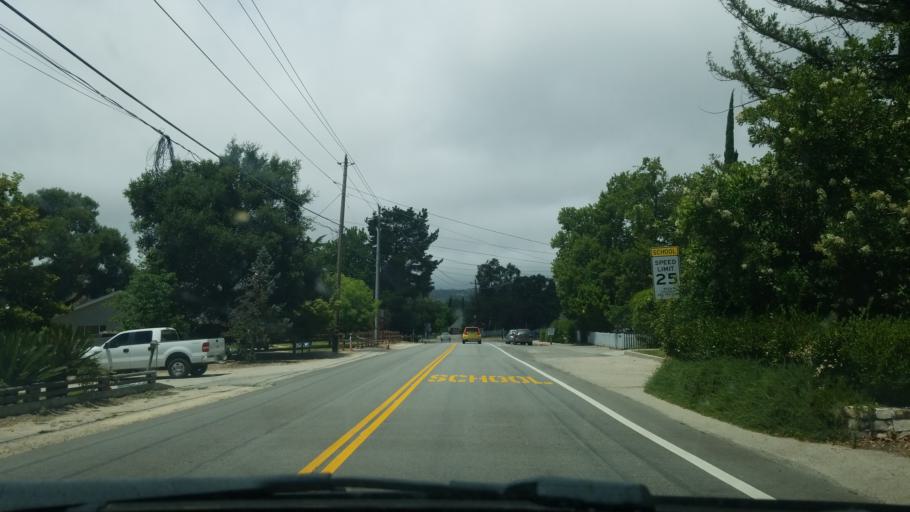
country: US
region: California
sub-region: San Luis Obispo County
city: Atascadero
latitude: 35.4644
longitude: -120.6548
